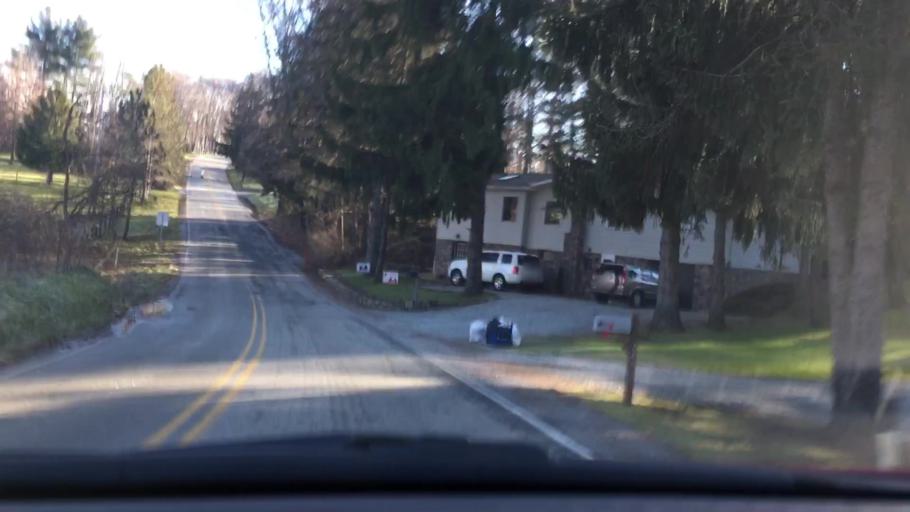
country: US
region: Pennsylvania
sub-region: Westmoreland County
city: Irwin
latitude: 40.3001
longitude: -79.6956
